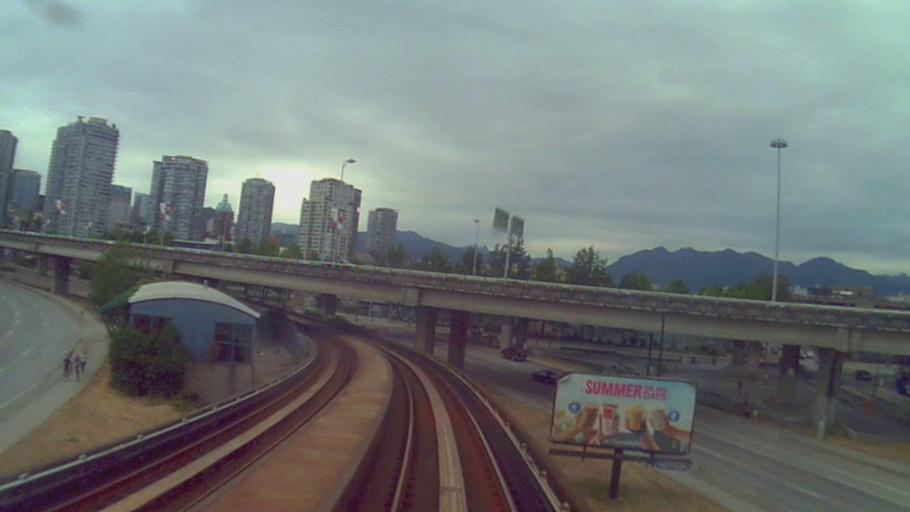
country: CA
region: British Columbia
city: West End
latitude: 49.2765
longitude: -123.1026
